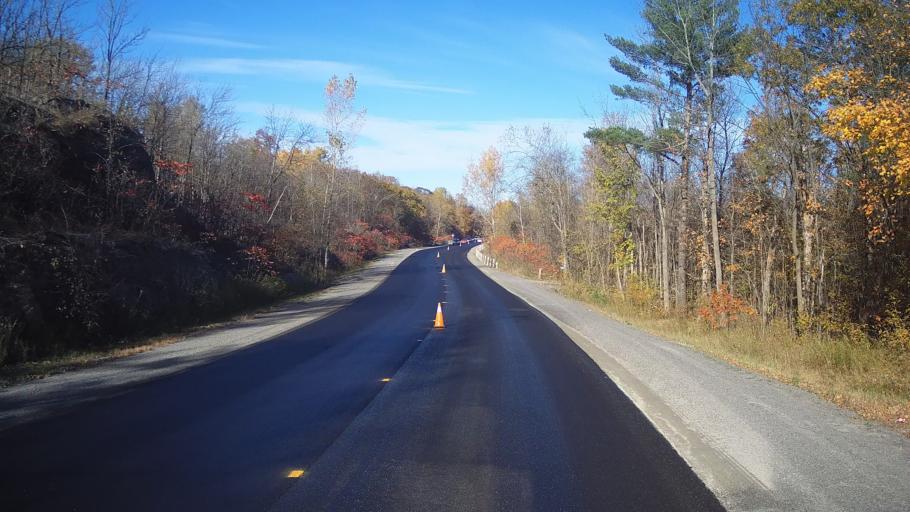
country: CA
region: Ontario
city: Kingston
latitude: 44.5116
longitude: -76.4678
